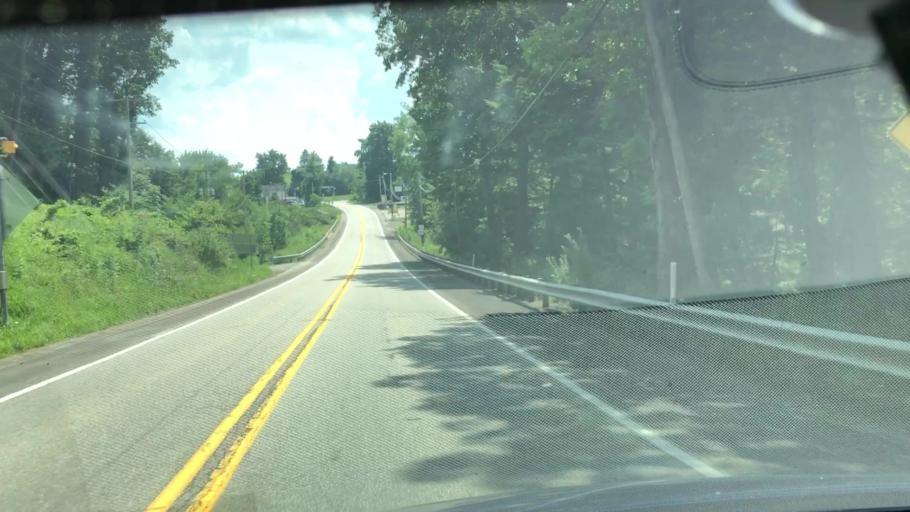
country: US
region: Pennsylvania
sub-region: Butler County
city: Saxonburg
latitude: 40.7223
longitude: -79.7563
